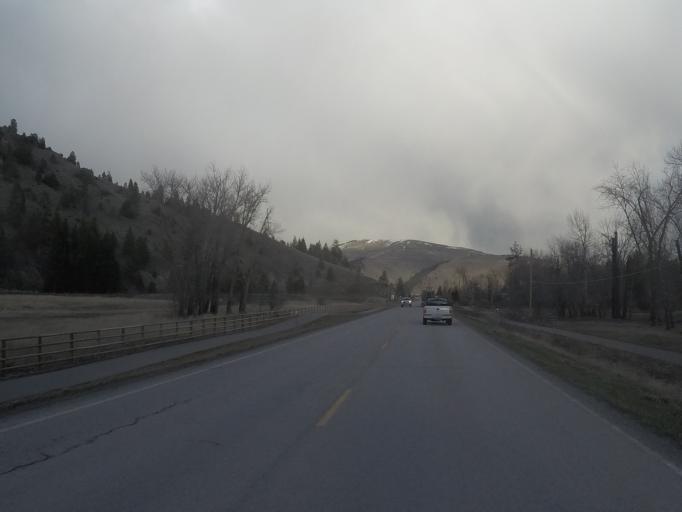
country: US
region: Montana
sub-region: Missoula County
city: Lolo
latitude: 46.7568
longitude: -114.1006
